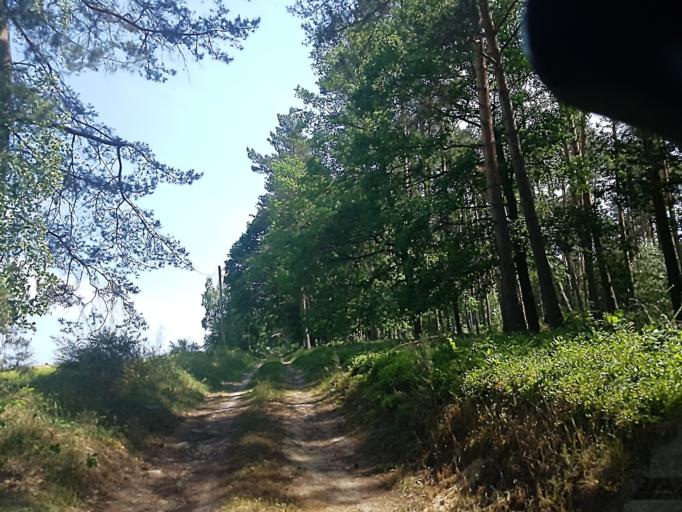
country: DE
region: Brandenburg
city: Gorzke
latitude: 52.1033
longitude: 12.3269
